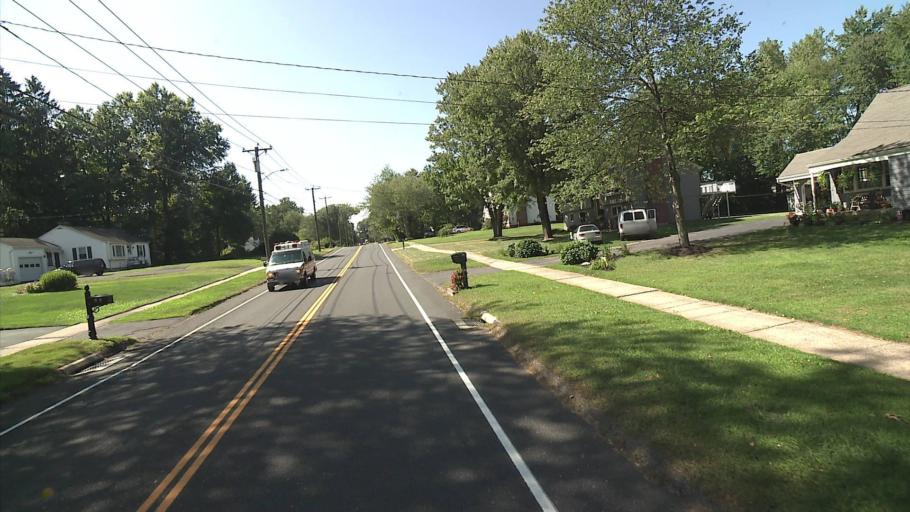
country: US
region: Connecticut
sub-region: Hartford County
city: Blue Hills
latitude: 41.8246
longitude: -72.7225
